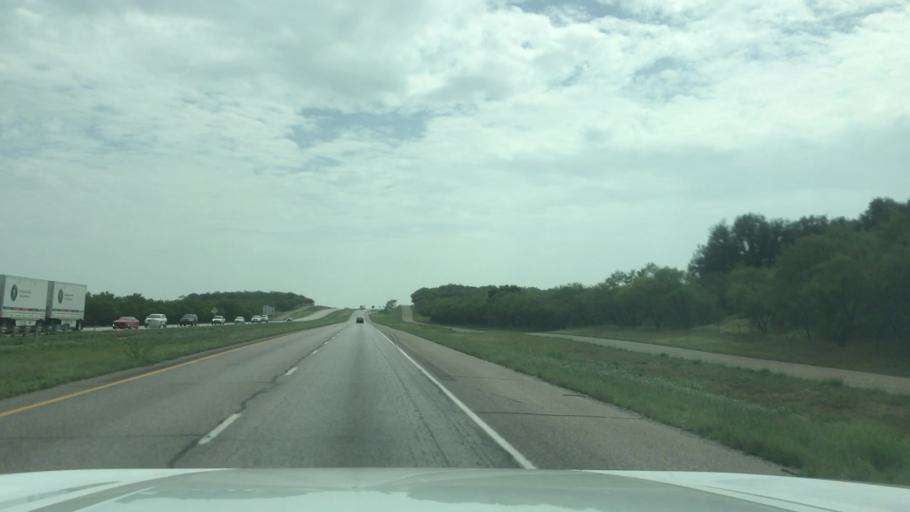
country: US
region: Texas
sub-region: Eastland County
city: Cisco
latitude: 32.3784
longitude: -99.1544
